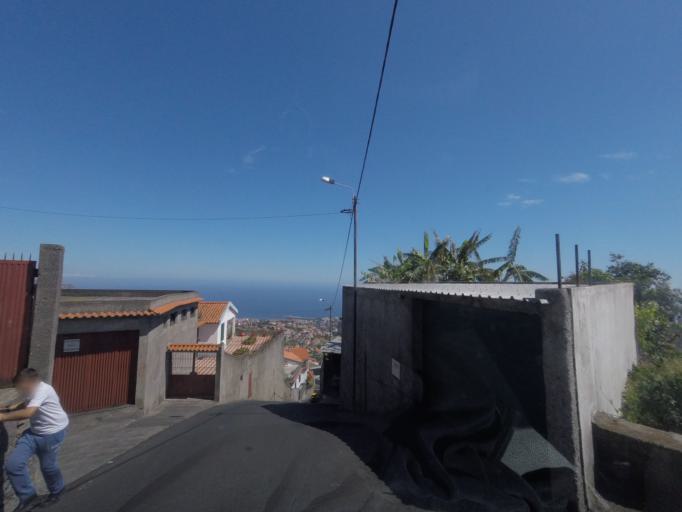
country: PT
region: Madeira
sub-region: Funchal
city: Nossa Senhora do Monte
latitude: 32.6743
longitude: -16.9332
